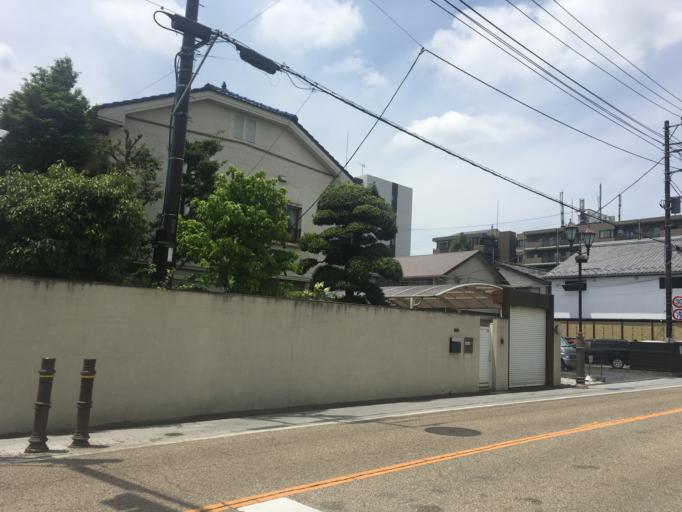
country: JP
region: Saitama
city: Shimotoda
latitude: 35.8255
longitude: 139.6784
